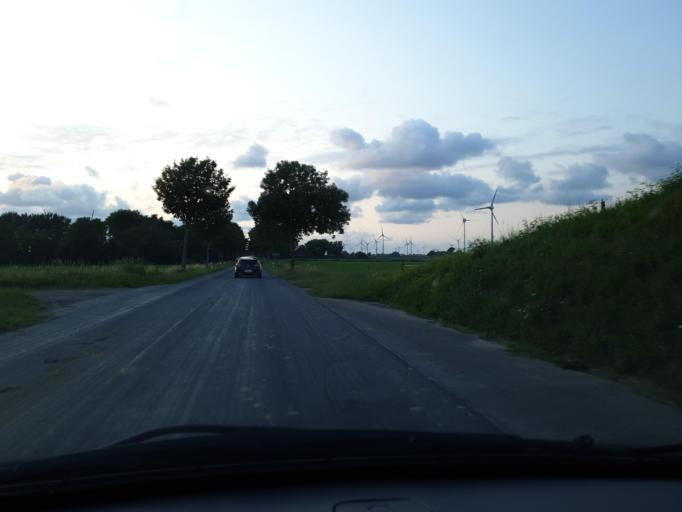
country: DE
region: Schleswig-Holstein
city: Kronprinzenkoog
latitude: 53.9548
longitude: 8.9360
